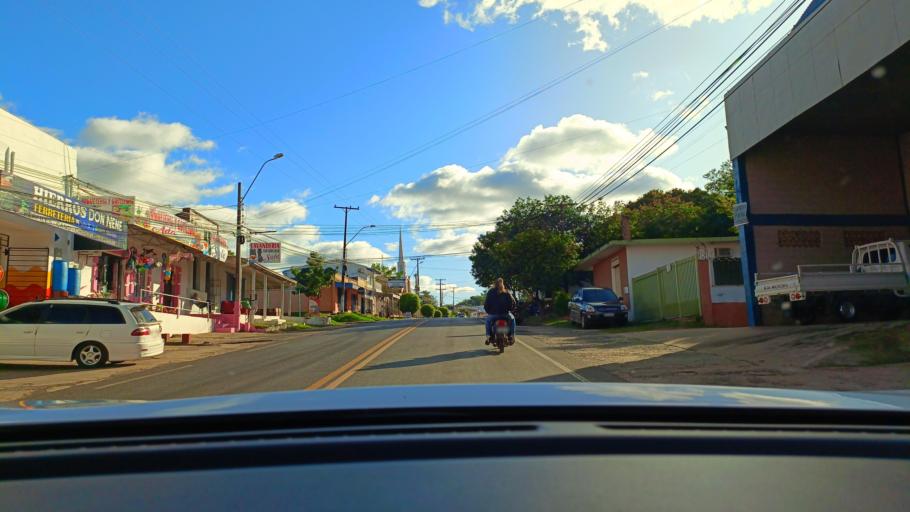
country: PY
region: San Pedro
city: Guayaybi
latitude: -24.6636
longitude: -56.4365
